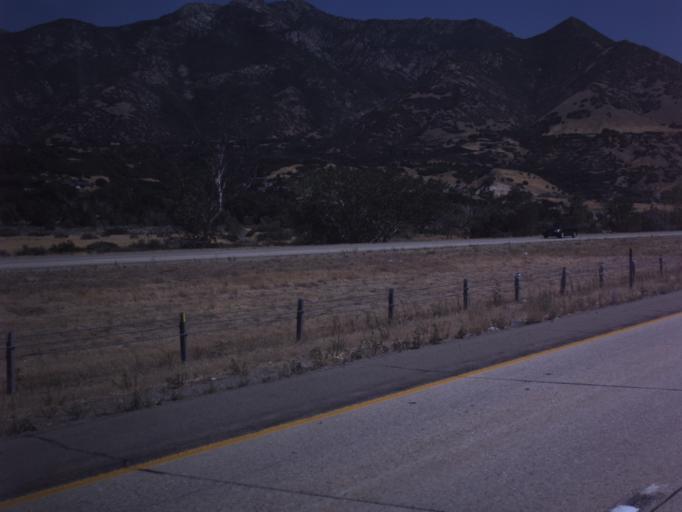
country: US
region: Utah
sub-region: Davis County
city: South Weber
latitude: 41.1363
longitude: -111.9274
